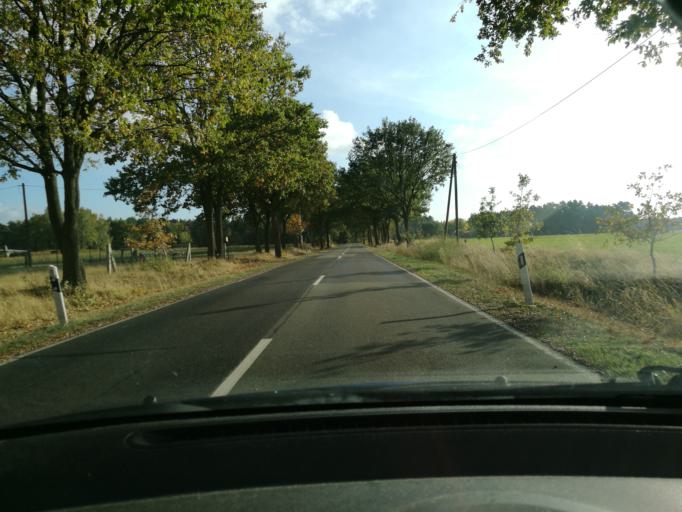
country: DE
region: Saxony-Anhalt
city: Luftkurort Arendsee
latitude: 52.8861
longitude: 11.4499
